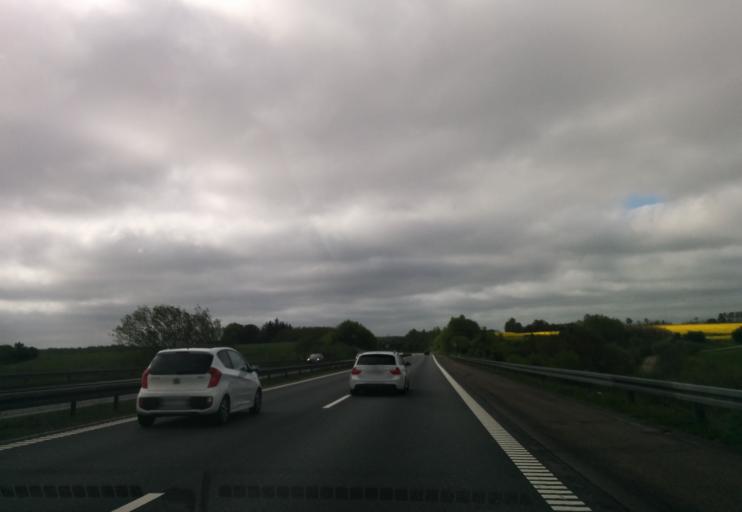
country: DK
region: South Denmark
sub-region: Fredericia Kommune
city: Taulov
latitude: 55.5726
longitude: 9.6154
